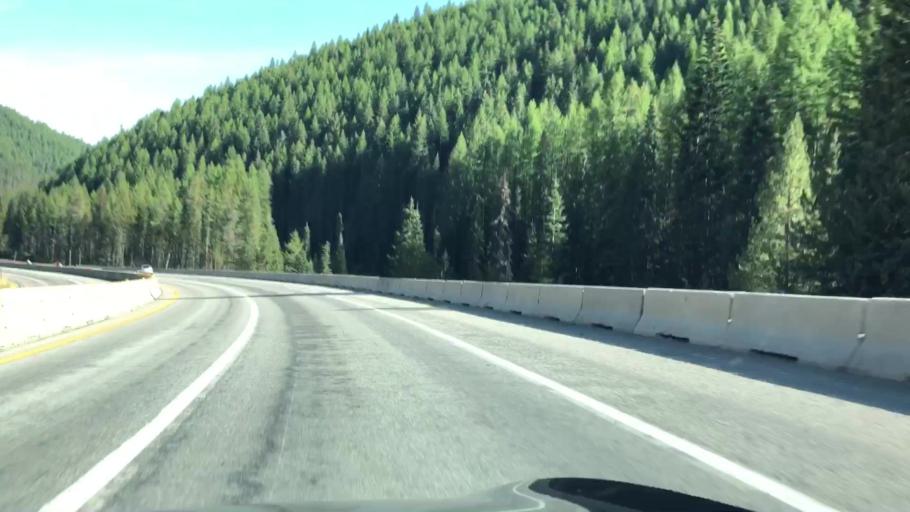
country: US
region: Idaho
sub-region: Shoshone County
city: Wallace
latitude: 47.4326
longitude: -115.6525
